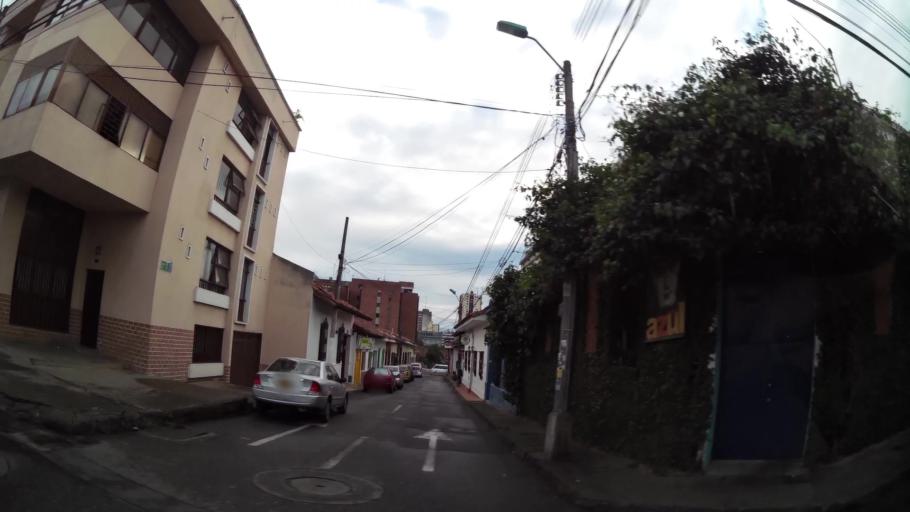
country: CO
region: Valle del Cauca
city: Cali
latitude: 3.4470
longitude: -76.5378
